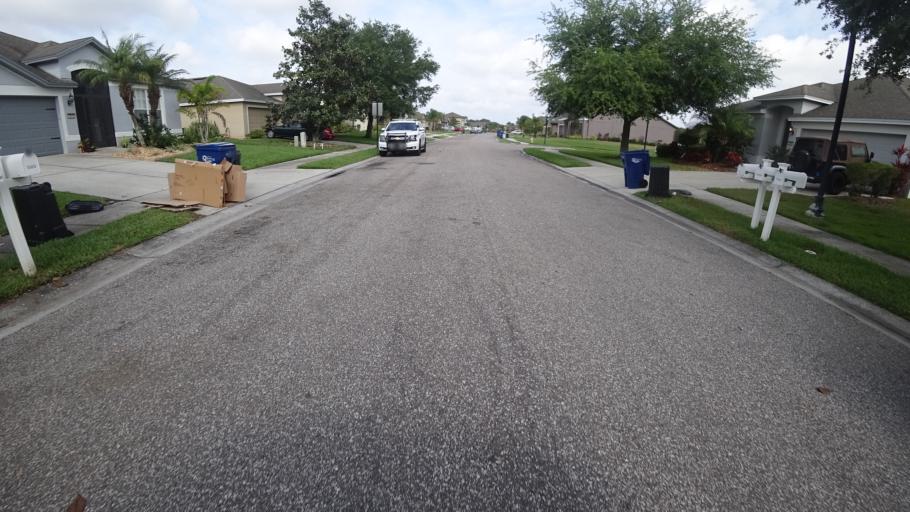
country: US
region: Florida
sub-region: Manatee County
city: Ellenton
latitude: 27.5679
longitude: -82.4644
